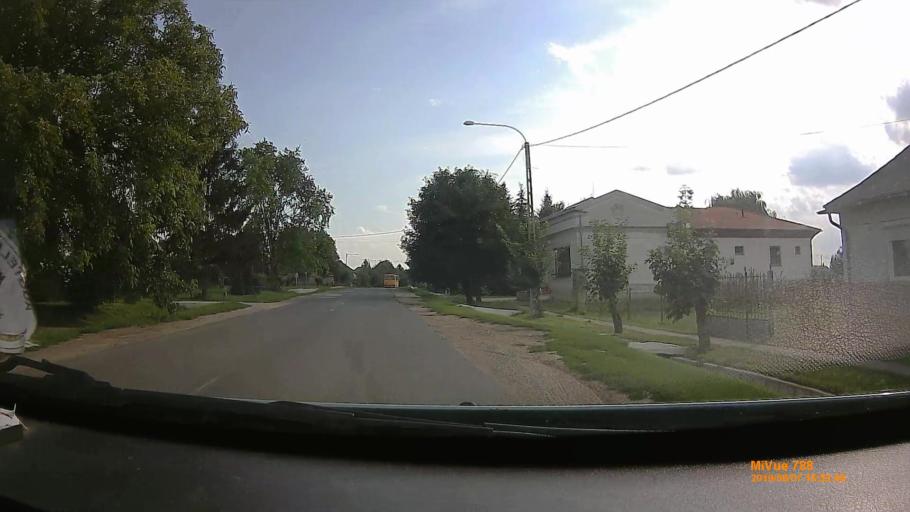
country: HU
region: Borsod-Abauj-Zemplen
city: Gonc
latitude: 48.3896
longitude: 21.2199
